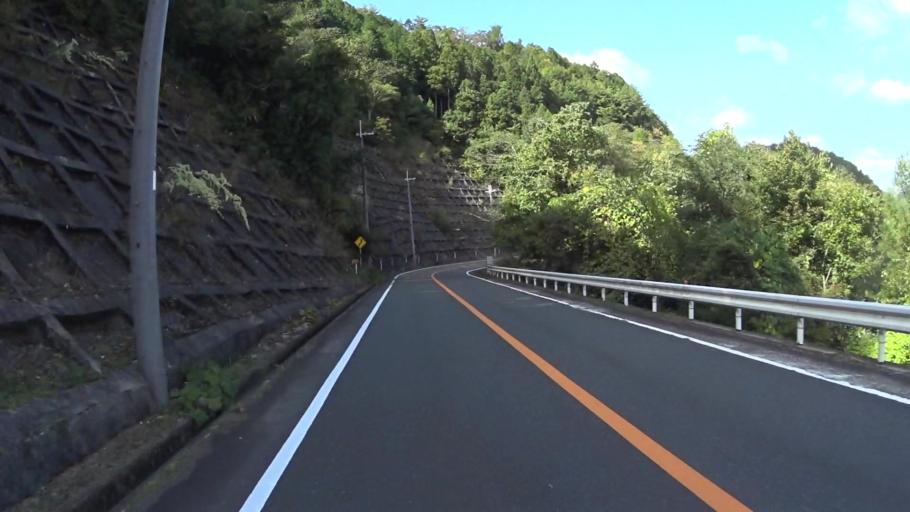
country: JP
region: Kyoto
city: Kameoka
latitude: 35.1300
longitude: 135.5418
